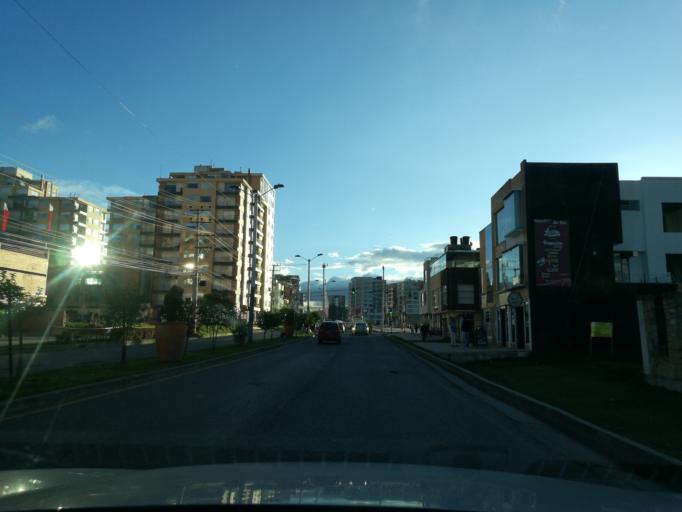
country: CO
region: Boyaca
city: Tunja
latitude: 5.5470
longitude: -73.3472
